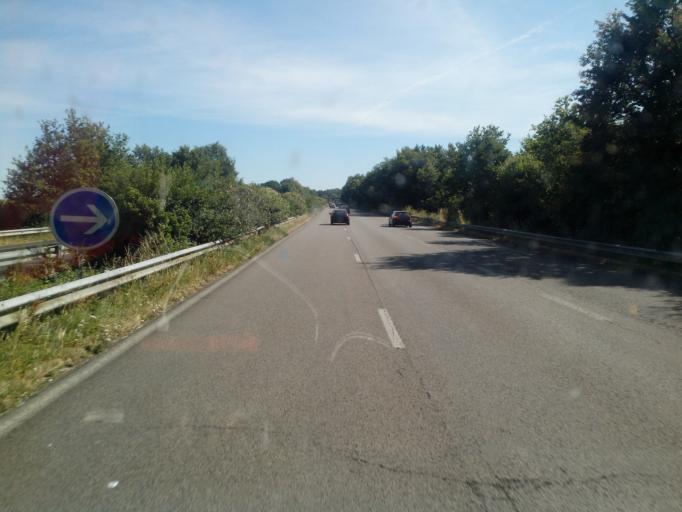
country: FR
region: Pays de la Loire
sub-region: Departement de la Loire-Atlantique
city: Nozay
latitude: 47.5750
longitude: -1.6309
